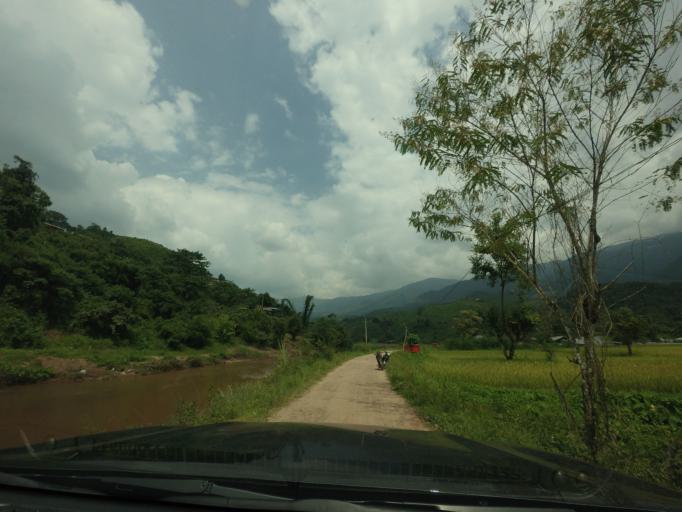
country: TH
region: Nan
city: Bo Kluea
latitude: 19.1936
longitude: 101.2013
